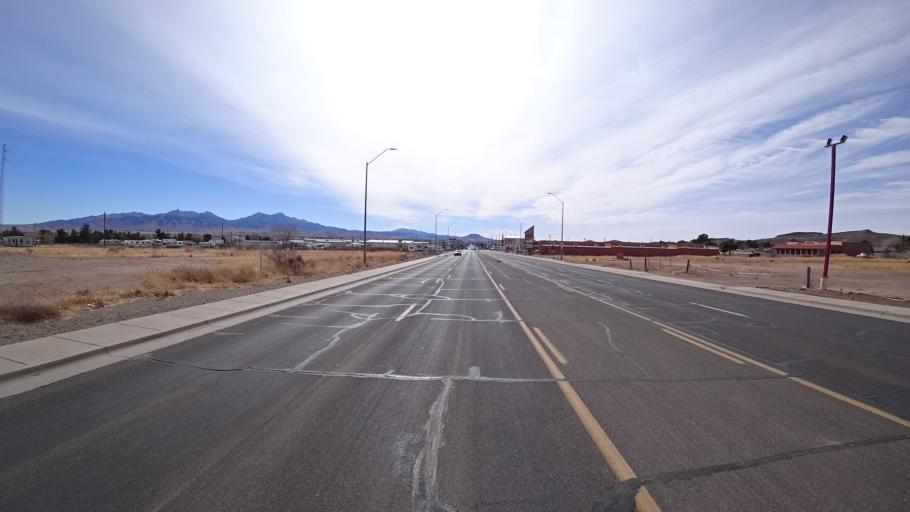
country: US
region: Arizona
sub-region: Mohave County
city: New Kingman-Butler
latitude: 35.2425
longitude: -114.0380
